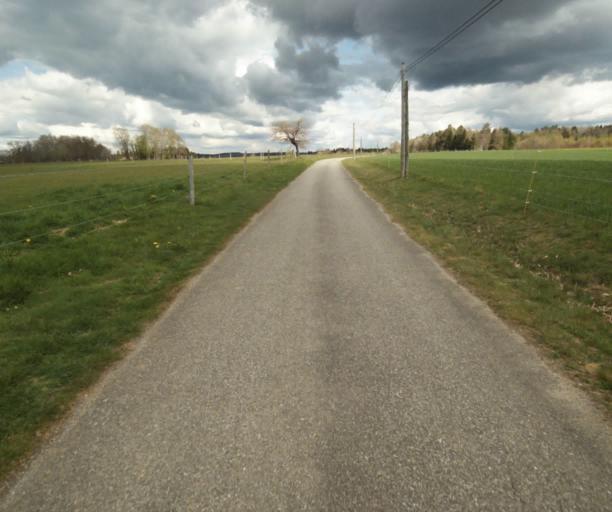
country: FR
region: Limousin
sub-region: Departement de la Correze
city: Laguenne
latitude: 45.2404
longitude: 1.8960
